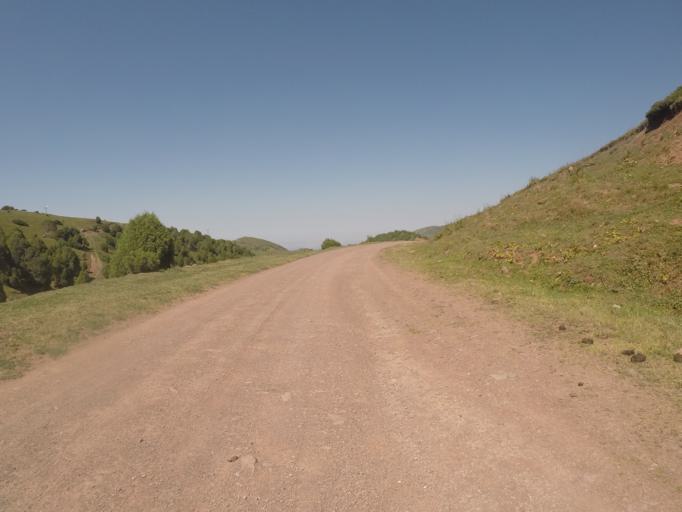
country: KG
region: Chuy
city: Bishkek
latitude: 42.6459
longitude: 74.5632
